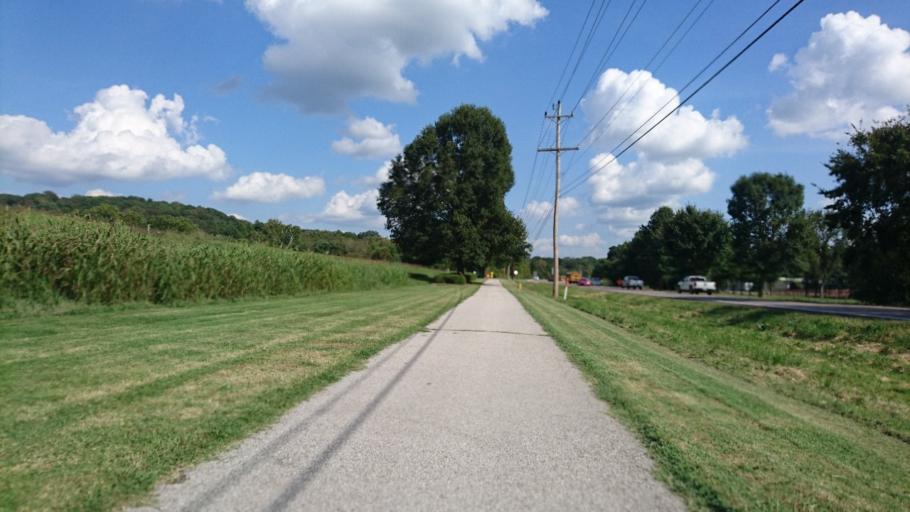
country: US
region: Missouri
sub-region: Saint Louis County
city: Wildwood
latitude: 38.5492
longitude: -90.6343
